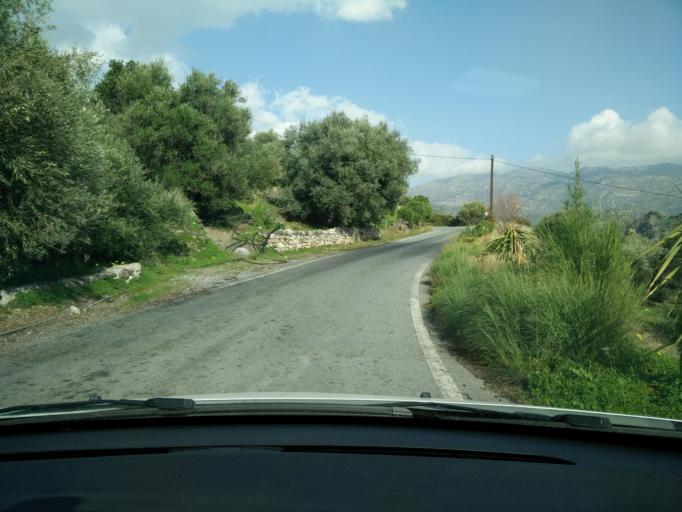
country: GR
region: Crete
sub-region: Nomos Lasithiou
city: Gra Liyia
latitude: 35.0333
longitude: 25.5751
